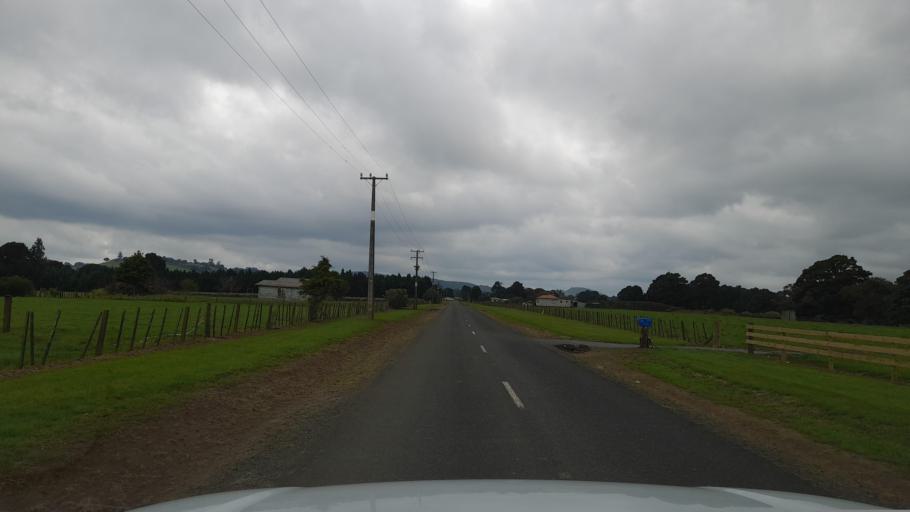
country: NZ
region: Northland
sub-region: Far North District
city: Waimate North
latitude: -35.4288
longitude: 173.7937
